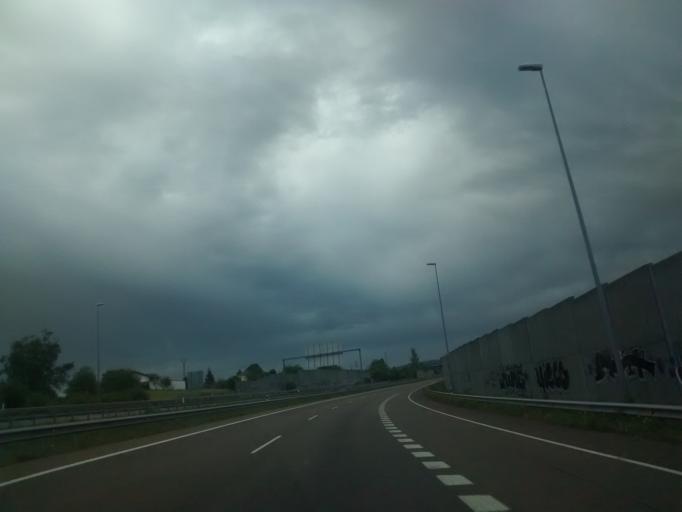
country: ES
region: Asturias
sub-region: Province of Asturias
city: Arriba
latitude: 43.5122
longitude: -5.5668
